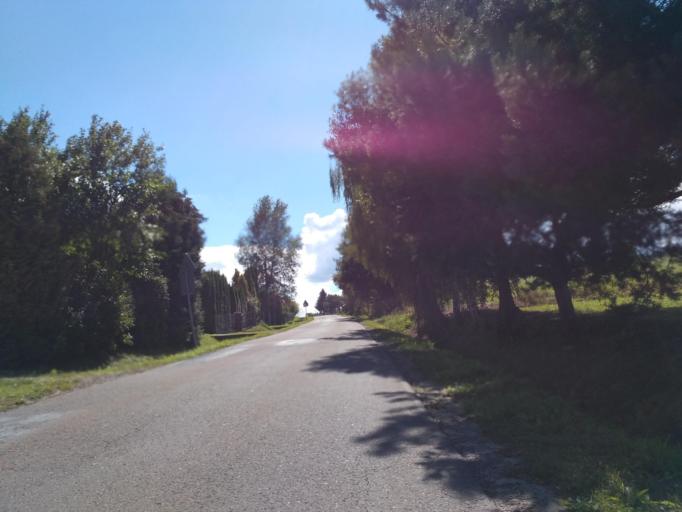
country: PL
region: Subcarpathian Voivodeship
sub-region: Powiat jasielski
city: Skolyszyn
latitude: 49.7901
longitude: 21.3415
